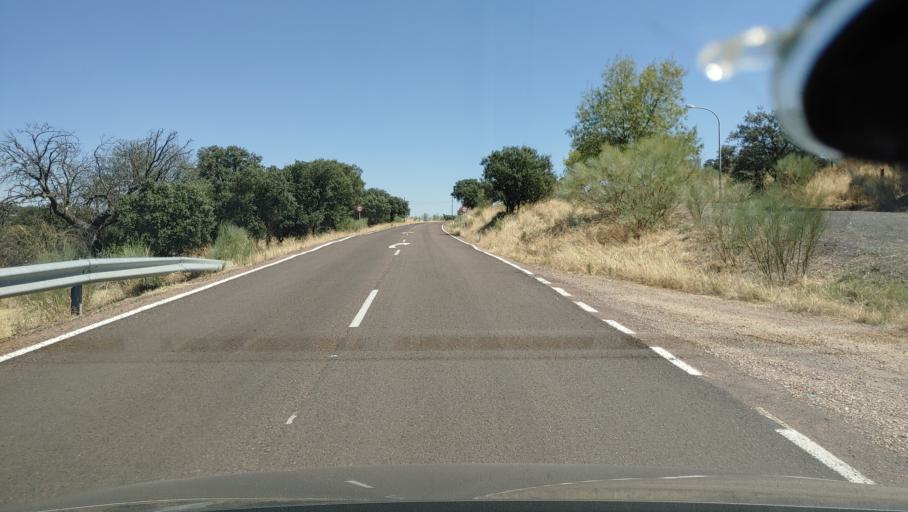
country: ES
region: Castille-La Mancha
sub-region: Provincia de Ciudad Real
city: Alamillo
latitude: 38.7403
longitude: -4.7222
